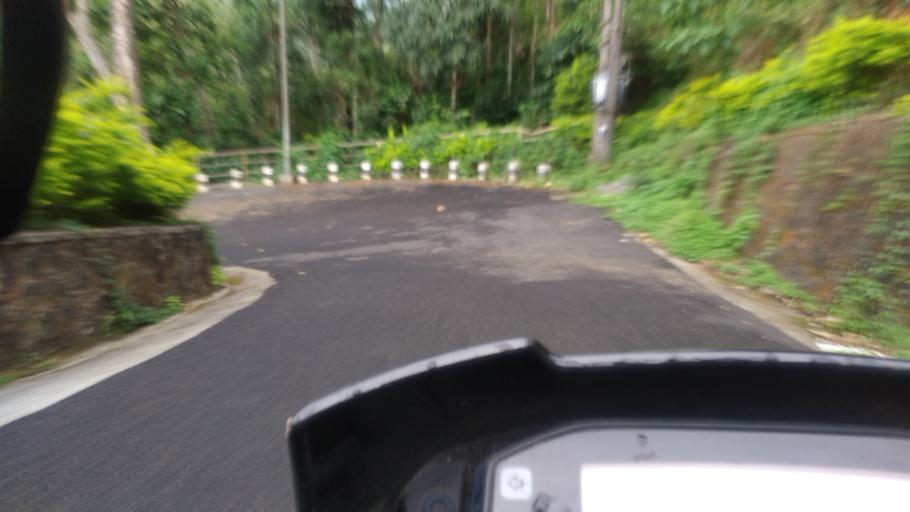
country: IN
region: Tamil Nadu
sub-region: Theni
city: Gudalur
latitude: 9.5843
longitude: 77.1199
